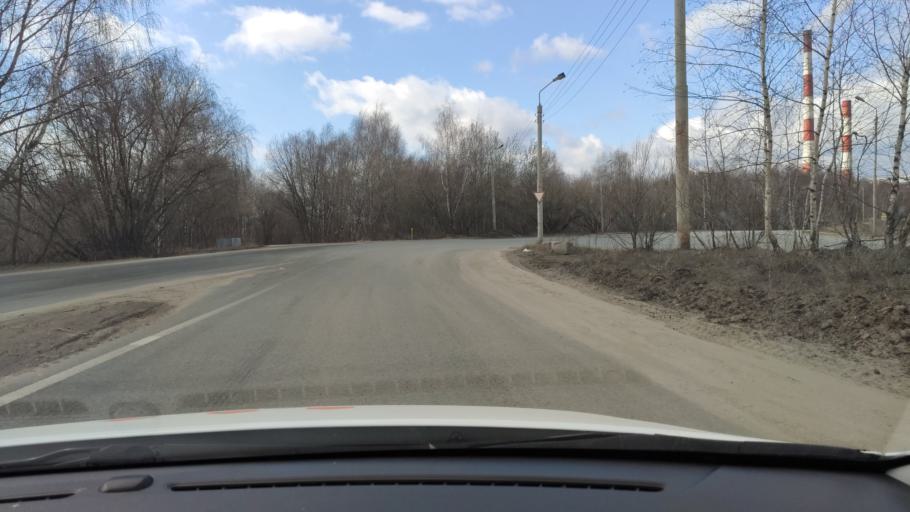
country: RU
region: Tatarstan
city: Staroye Arakchino
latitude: 55.8620
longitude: 48.9648
